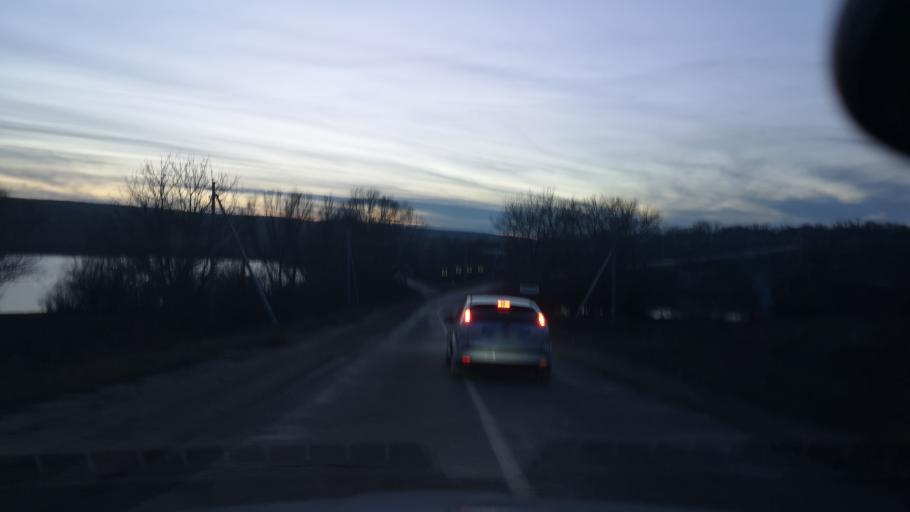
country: MD
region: Orhei
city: Orhei
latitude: 47.2860
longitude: 28.8762
